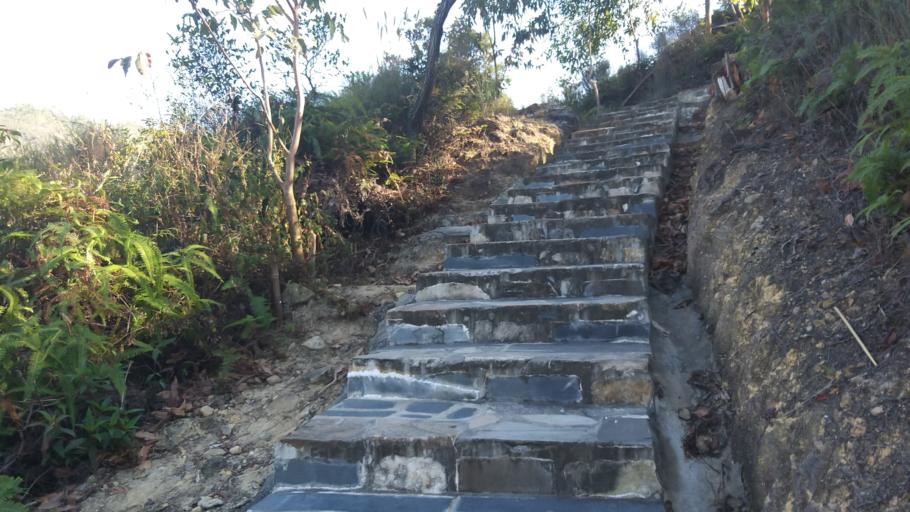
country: HK
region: Tuen Mun
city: Tuen Mun
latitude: 22.4049
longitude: 113.9885
